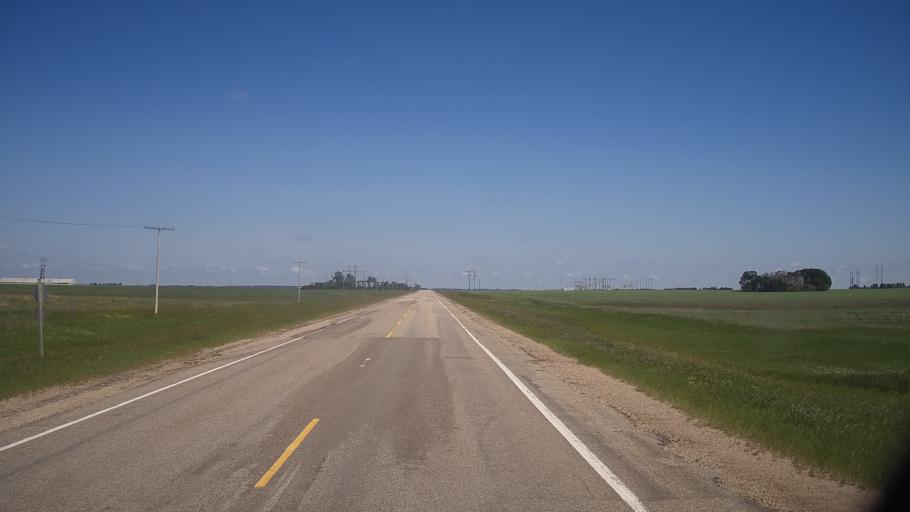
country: CA
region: Saskatchewan
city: Saskatoon
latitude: 51.9734
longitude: -106.0753
